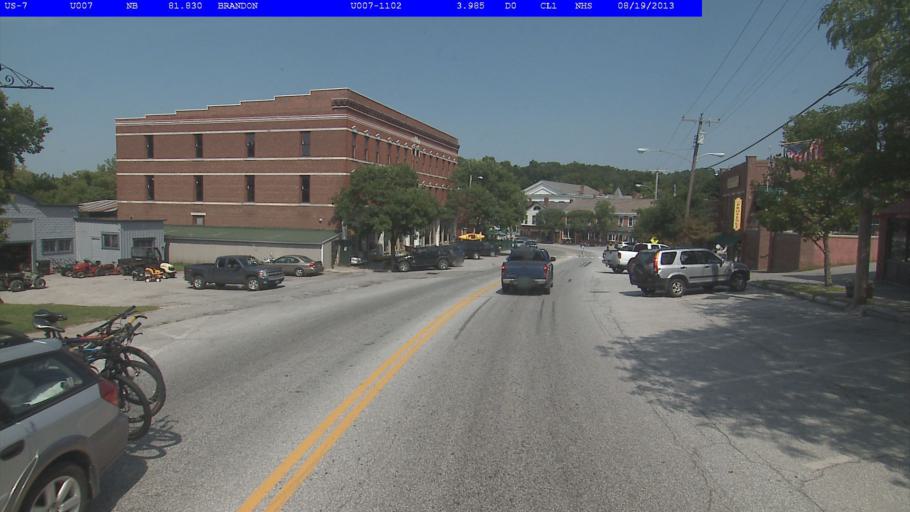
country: US
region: Vermont
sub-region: Rutland County
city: Brandon
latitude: 43.7984
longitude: -73.0883
